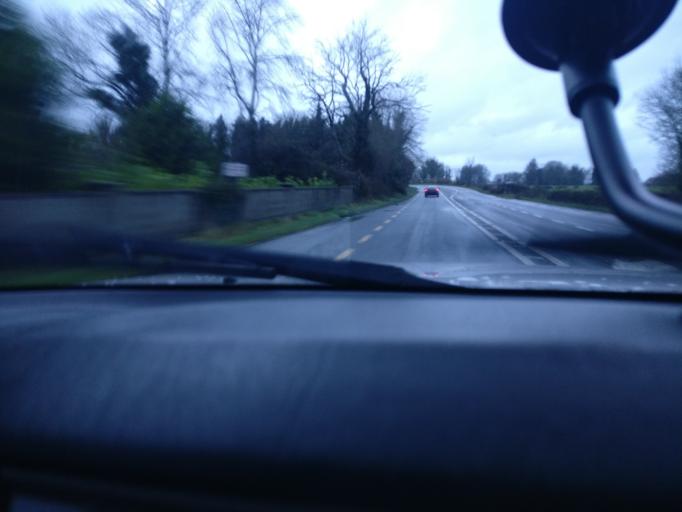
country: IE
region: Connaught
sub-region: County Galway
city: Ballinasloe
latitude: 53.3117
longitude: -8.2811
